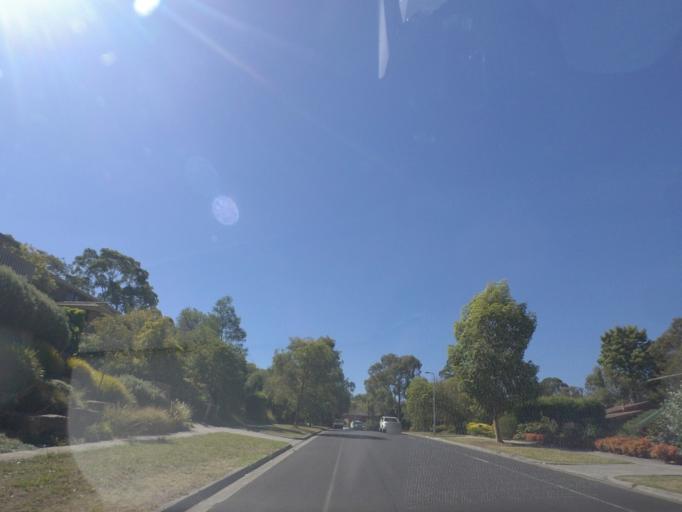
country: AU
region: Victoria
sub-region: Manningham
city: Park Orchards
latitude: -37.7948
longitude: 145.2246
